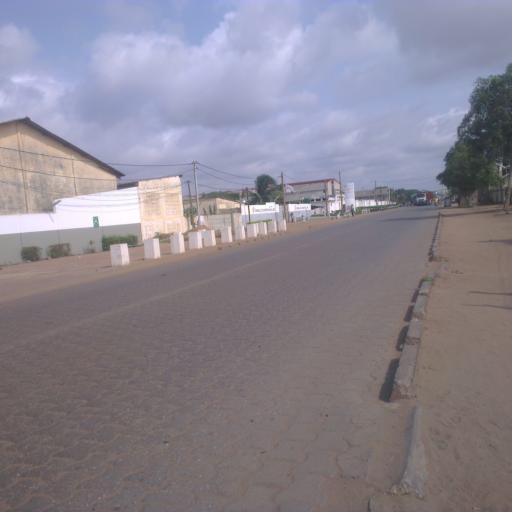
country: TG
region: Maritime
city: Lome
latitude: 6.1488
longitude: 1.2727
